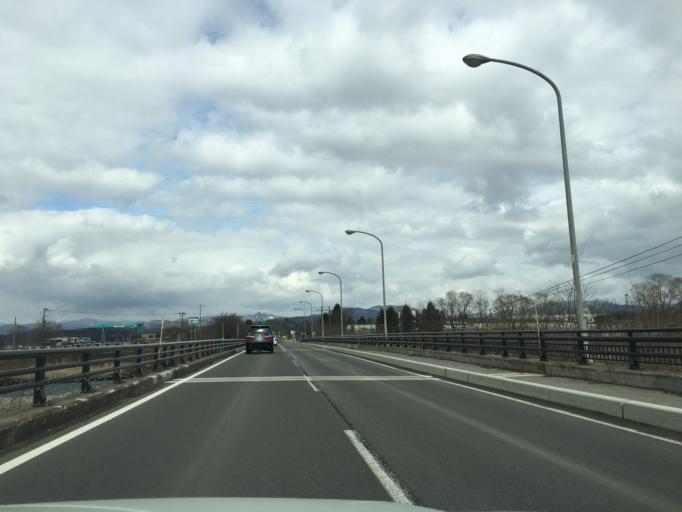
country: JP
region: Akita
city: Hanawa
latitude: 40.2535
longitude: 140.7597
